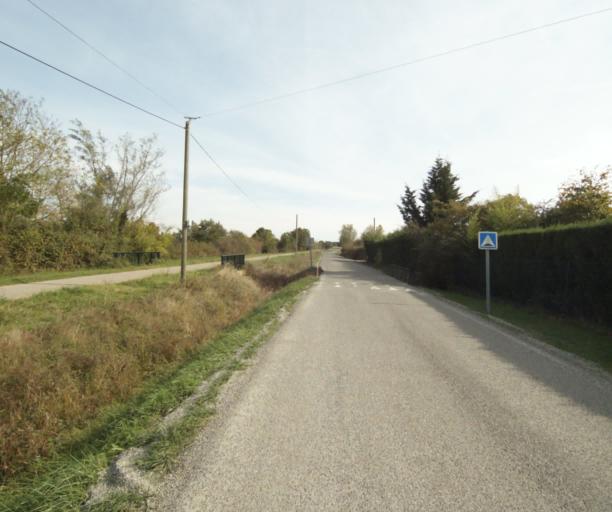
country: FR
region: Midi-Pyrenees
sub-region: Departement du Tarn-et-Garonne
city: Labastide-Saint-Pierre
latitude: 43.9132
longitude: 1.3770
